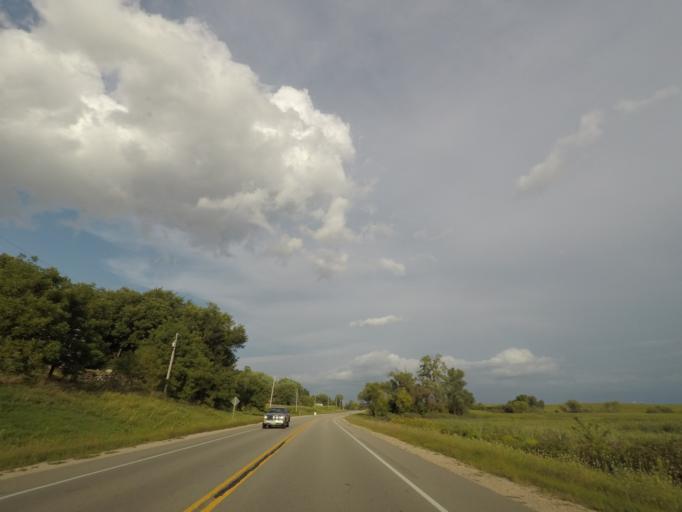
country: US
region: Wisconsin
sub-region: Dane County
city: Waunakee
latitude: 43.1886
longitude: -89.4975
